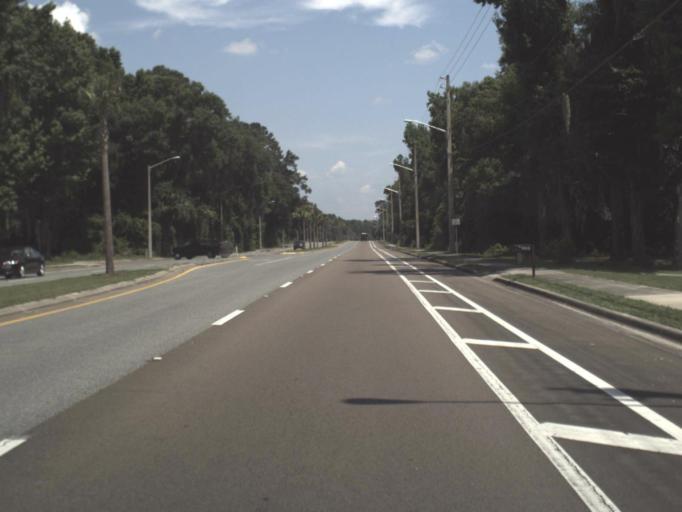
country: US
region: Florida
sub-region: Alachua County
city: Gainesville
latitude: 29.6306
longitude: -82.2648
